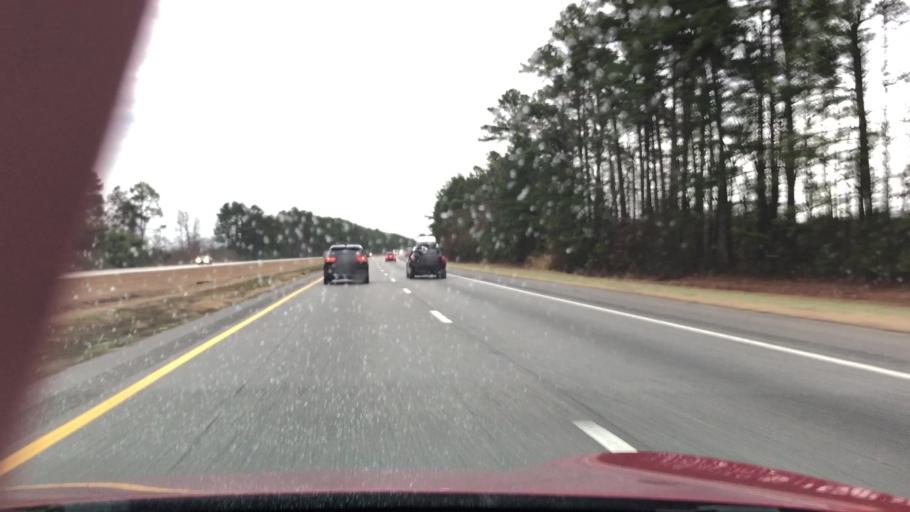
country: US
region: South Carolina
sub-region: Dillon County
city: Latta
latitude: 34.3705
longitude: -79.4912
